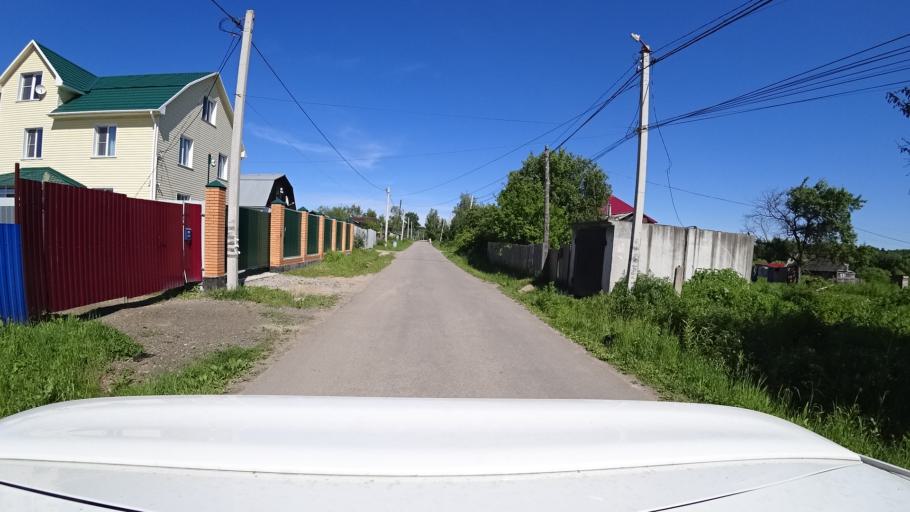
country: RU
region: Khabarovsk Krai
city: Topolevo
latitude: 48.5524
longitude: 135.1944
